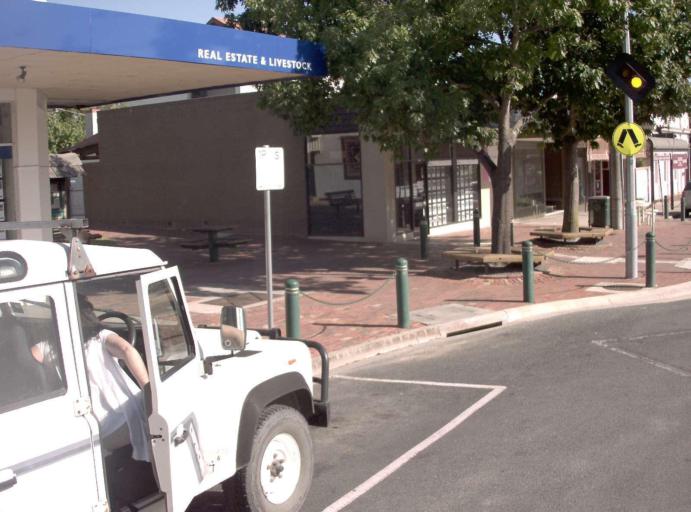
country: AU
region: Victoria
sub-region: East Gippsland
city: Lakes Entrance
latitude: -37.7064
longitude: 148.4552
